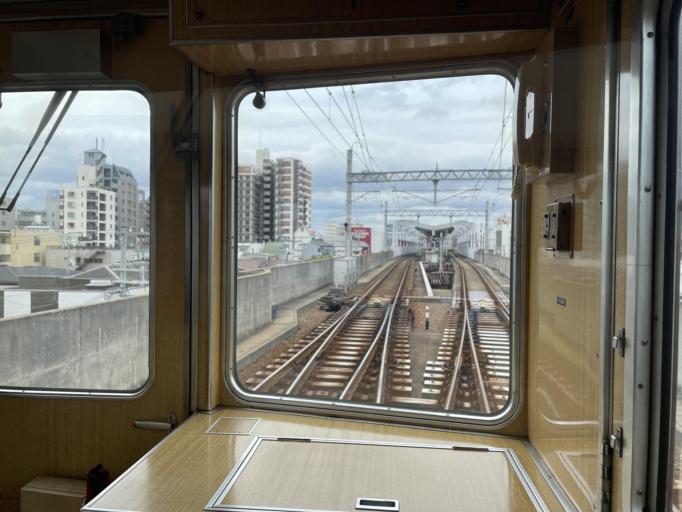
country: JP
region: Hyogo
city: Nishinomiya-hama
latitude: 34.7333
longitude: 135.3524
